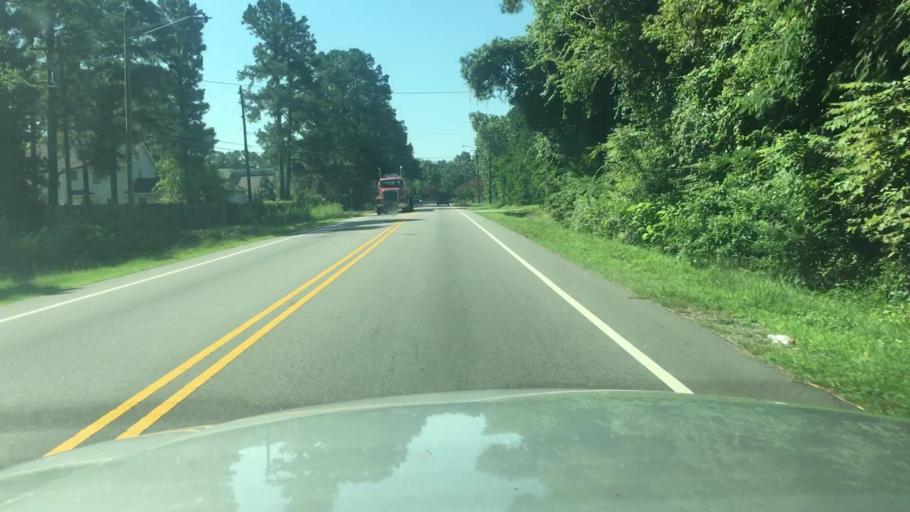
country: US
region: North Carolina
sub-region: Cumberland County
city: Fayetteville
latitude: 35.1083
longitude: -78.9023
